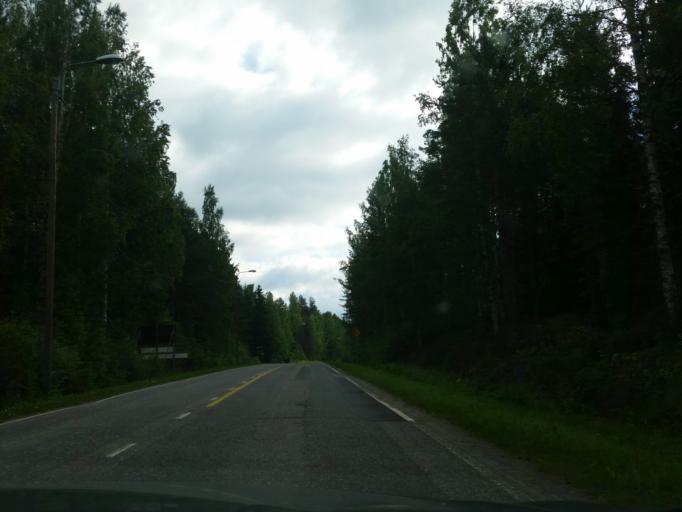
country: FI
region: Northern Savo
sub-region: Sisae-Savo
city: Tervo
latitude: 62.9572
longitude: 26.7644
